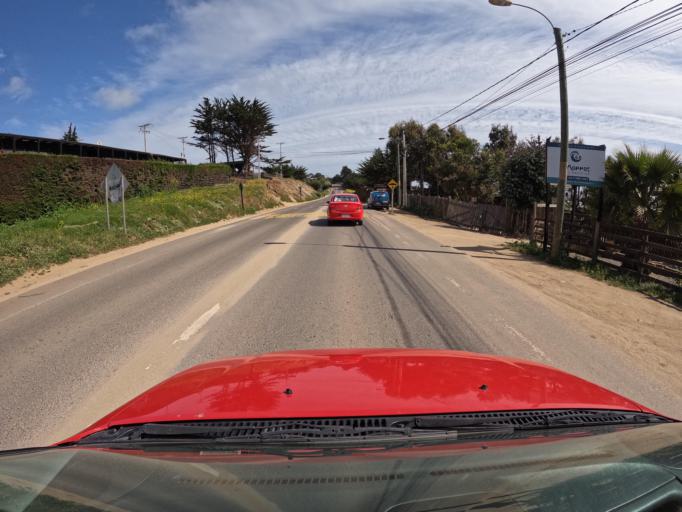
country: CL
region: O'Higgins
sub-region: Provincia de Colchagua
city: Santa Cruz
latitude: -34.4171
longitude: -72.0298
